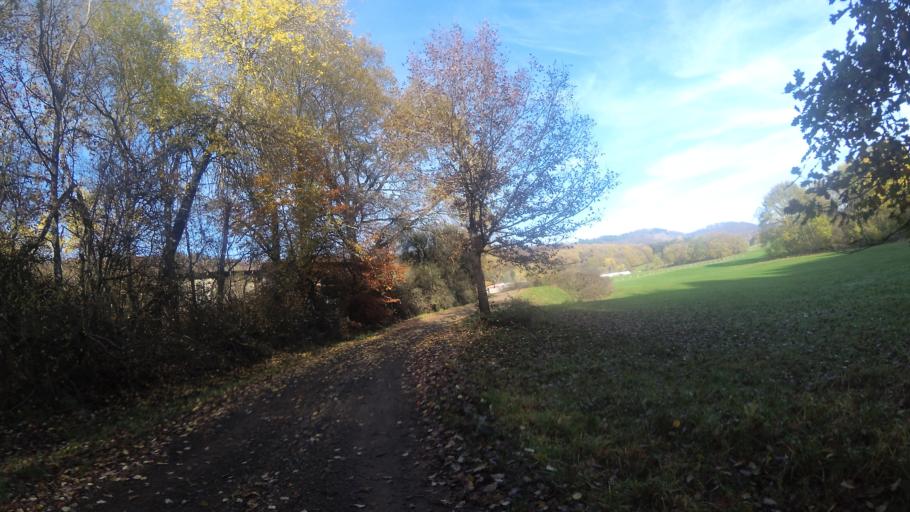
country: DE
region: Saarland
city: Freisen
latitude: 49.5331
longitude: 7.2524
